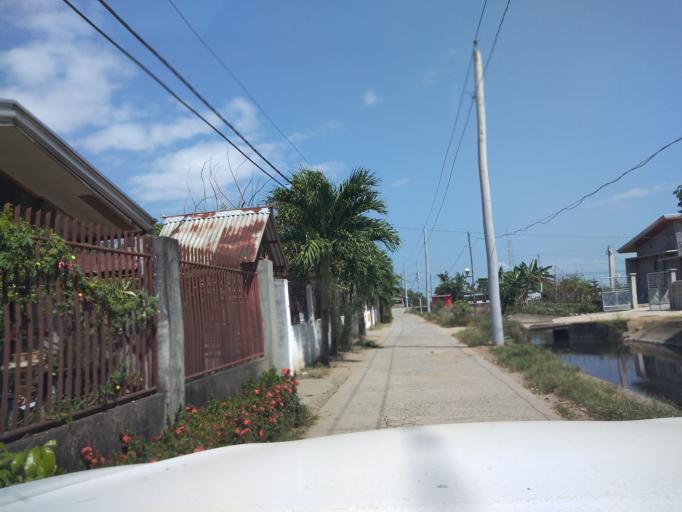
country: PH
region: Central Luzon
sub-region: Province of Pampanga
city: Talang
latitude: 15.0245
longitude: 120.8382
